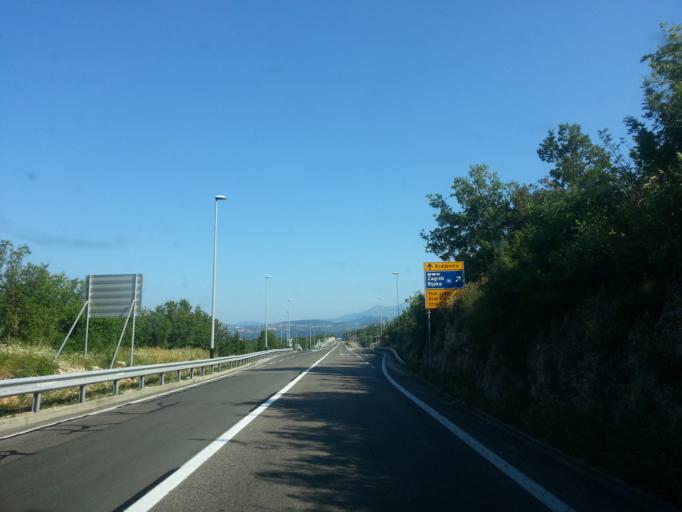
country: HR
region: Primorsko-Goranska
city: Hreljin
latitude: 45.2571
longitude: 14.5929
